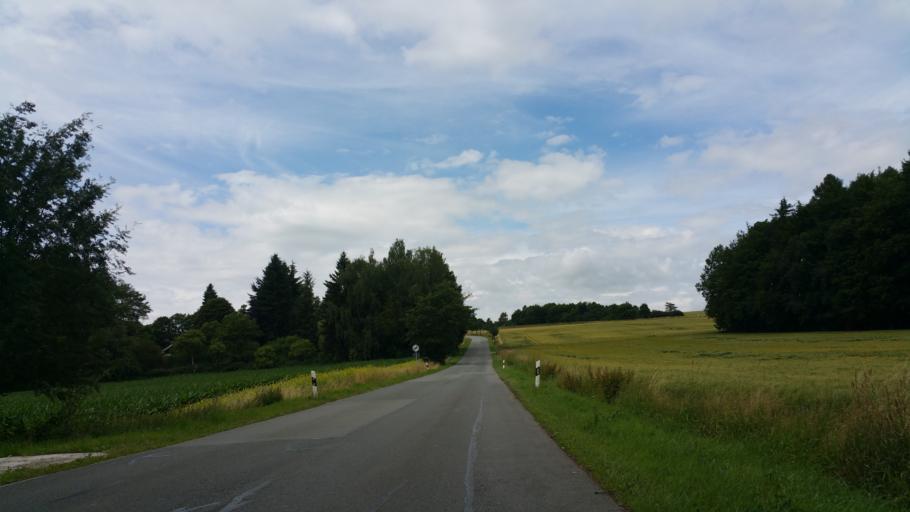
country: DE
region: Bavaria
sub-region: Upper Franconia
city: Schwarzenbach an der Saale
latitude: 50.2218
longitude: 11.9200
